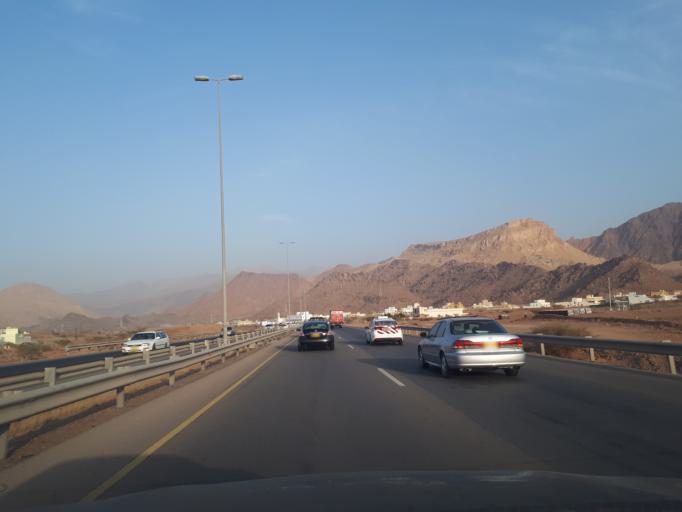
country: OM
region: Muhafazat ad Dakhiliyah
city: Bidbid
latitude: 23.4605
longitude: 58.1657
